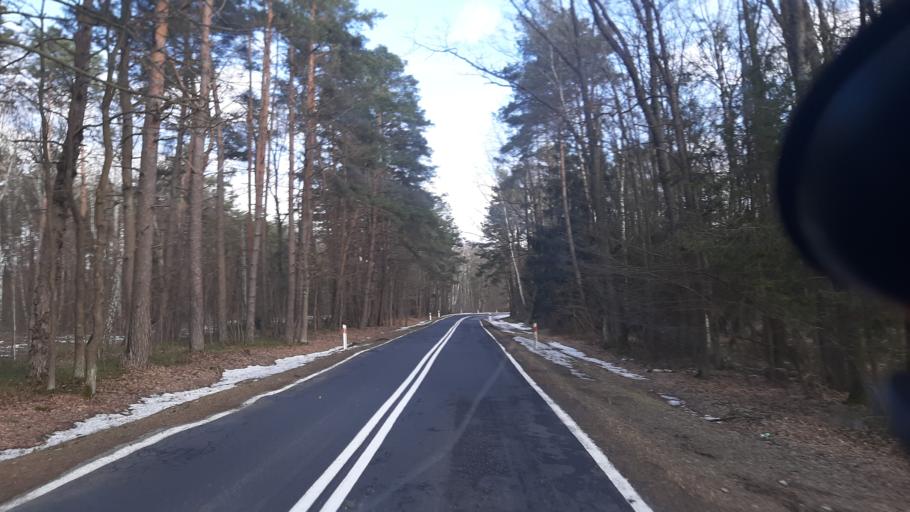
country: PL
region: Lublin Voivodeship
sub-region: Powiat wlodawski
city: Urszulin
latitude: 51.4988
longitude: 23.1960
